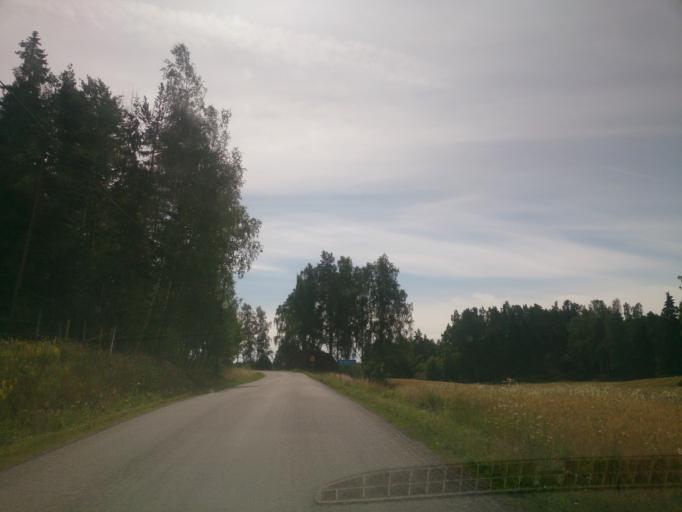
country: SE
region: OEstergoetland
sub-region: Valdemarsviks Kommun
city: Gusum
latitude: 58.3135
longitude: 16.3356
